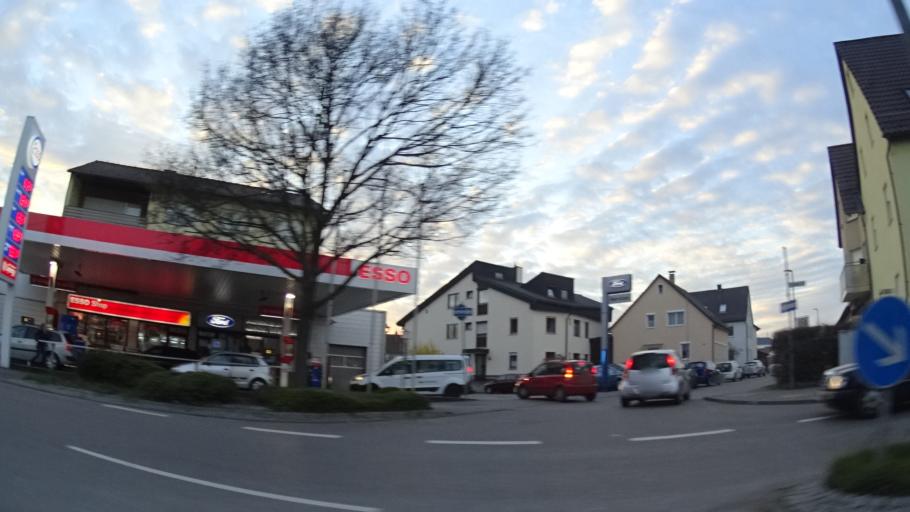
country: DE
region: Baden-Wuerttemberg
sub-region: Regierungsbezirk Stuttgart
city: Markgroningen
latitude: 48.9062
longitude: 9.0836
